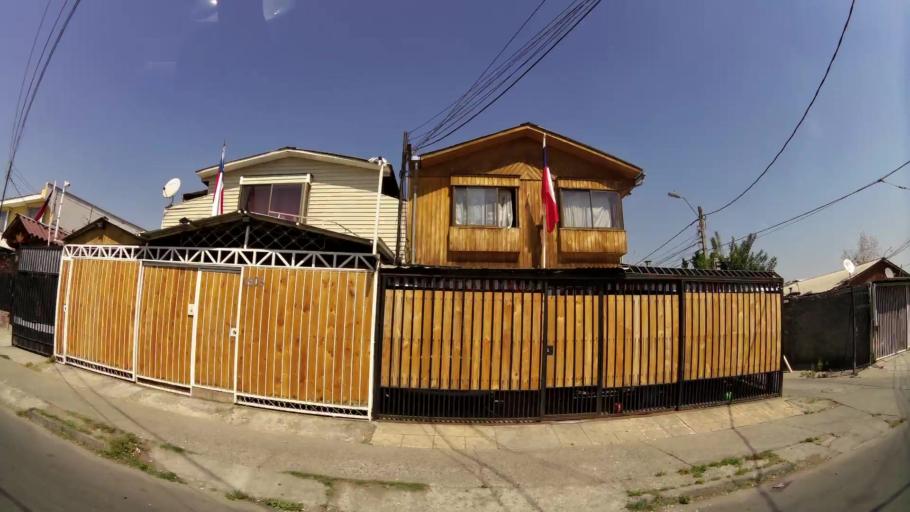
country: CL
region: Santiago Metropolitan
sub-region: Provincia de Santiago
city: La Pintana
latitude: -33.5520
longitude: -70.6111
